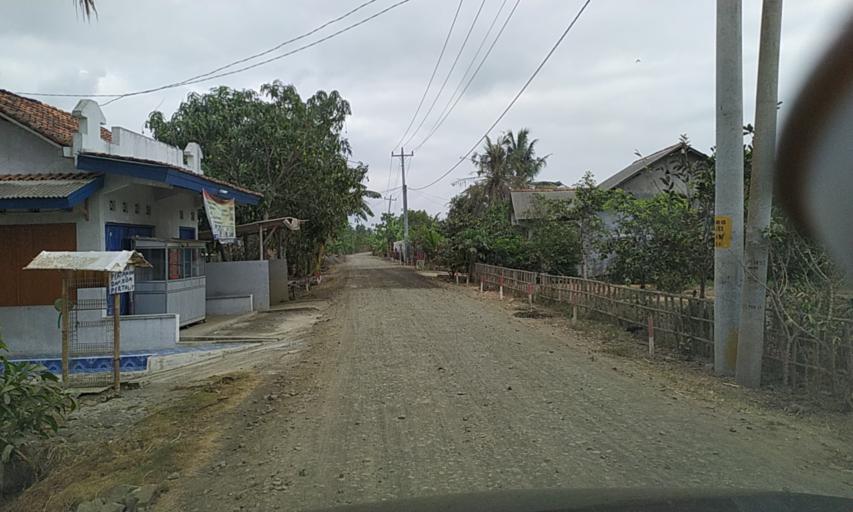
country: ID
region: Central Java
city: Jeruklegi
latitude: -7.6476
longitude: 108.9479
